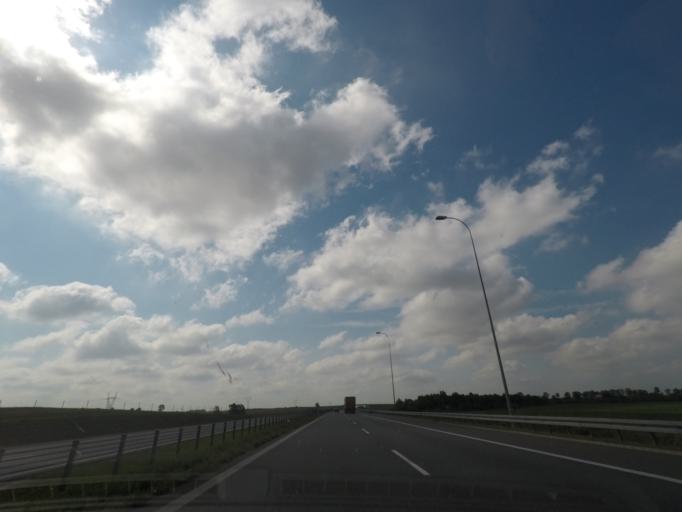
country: PL
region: Kujawsko-Pomorskie
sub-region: Powiat chelminski
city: Lisewo
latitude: 53.2529
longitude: 18.7256
